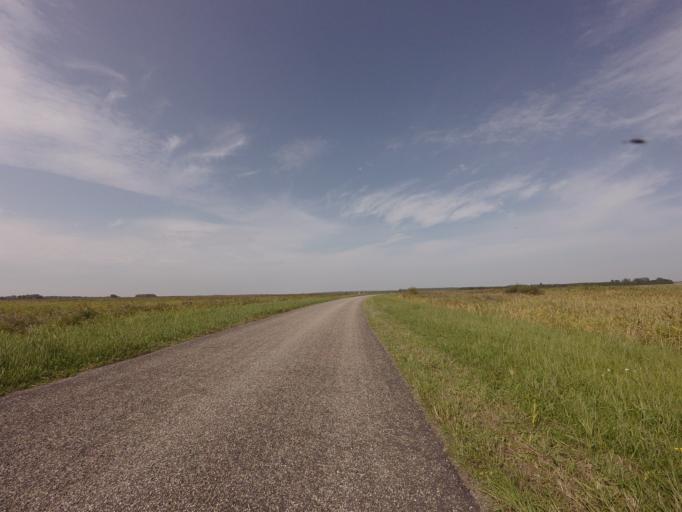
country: NL
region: Groningen
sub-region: Gemeente De Marne
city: Ulrum
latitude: 53.3479
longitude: 6.2682
